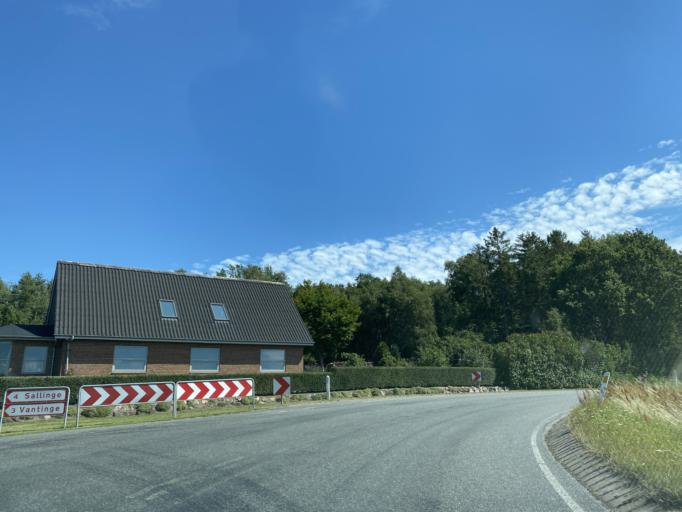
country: DK
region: South Denmark
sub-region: Faaborg-Midtfyn Kommune
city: Ringe
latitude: 55.2101
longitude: 10.3951
